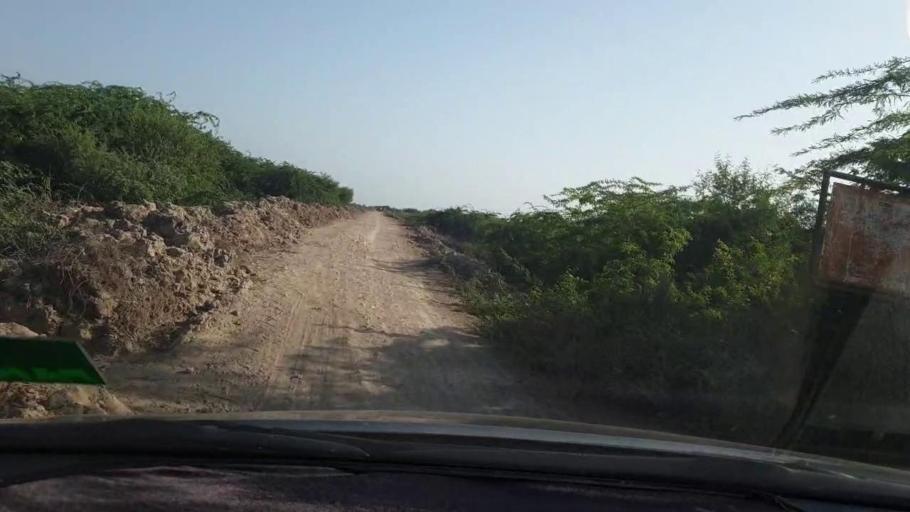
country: PK
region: Sindh
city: Naukot
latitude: 24.9109
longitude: 69.2766
